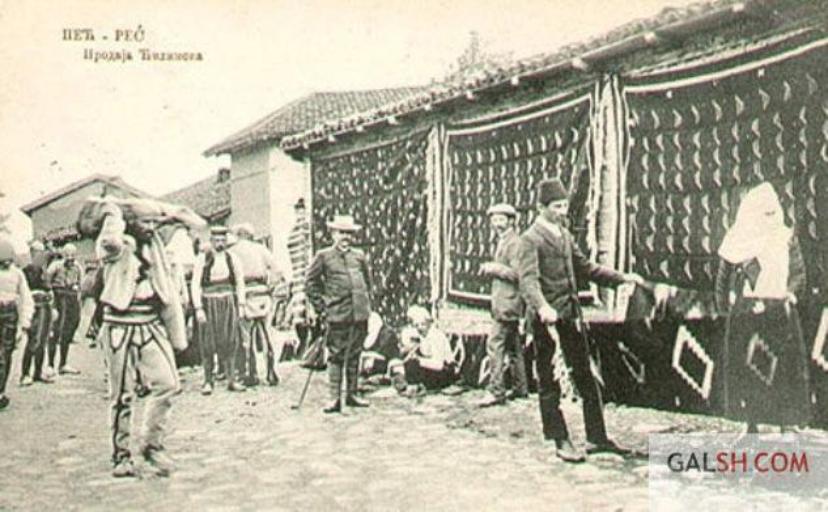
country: XK
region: Pec
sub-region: Komuna e Pejes
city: Peje
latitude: 42.6604
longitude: 20.2953
